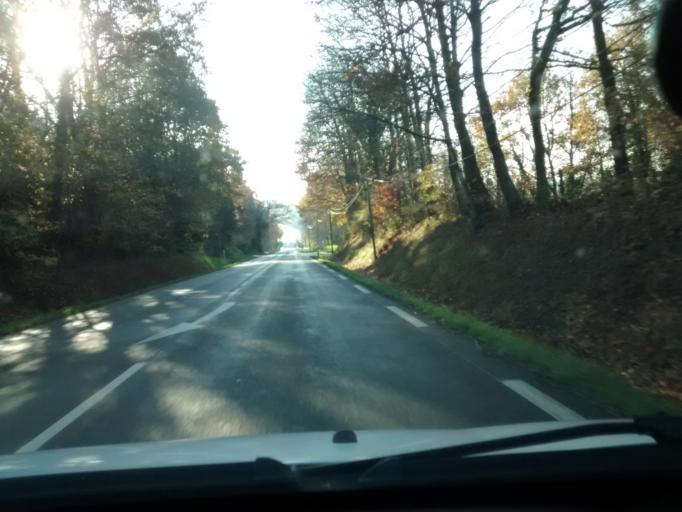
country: FR
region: Brittany
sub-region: Departement d'Ille-et-Vilaine
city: Sens-de-Bretagne
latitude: 48.3677
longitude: -1.5007
